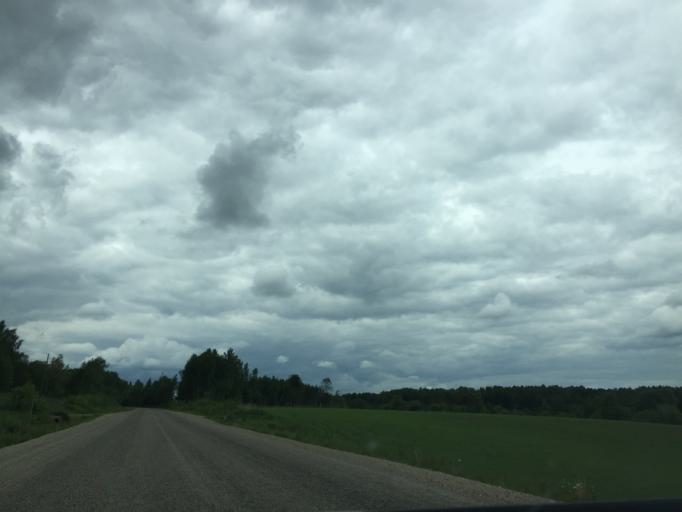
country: LV
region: Dagda
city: Dagda
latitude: 56.0659
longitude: 27.5608
